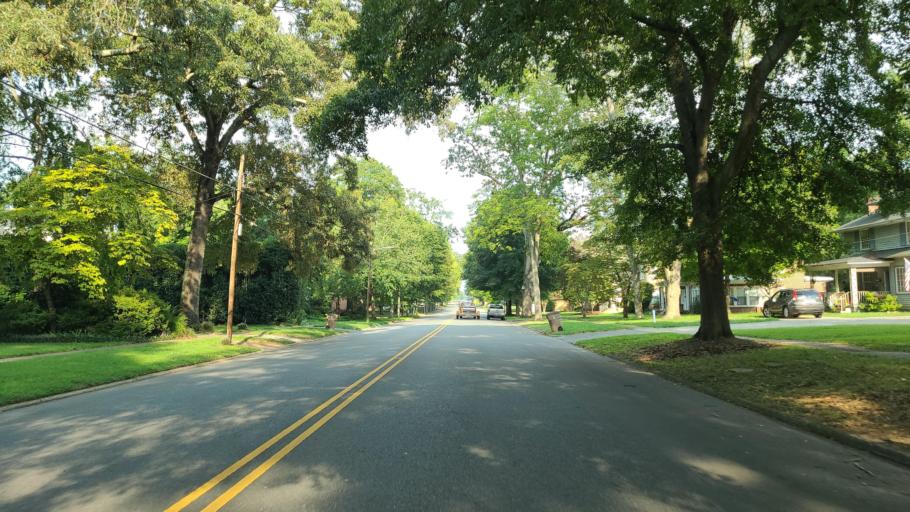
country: US
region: North Carolina
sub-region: Cleveland County
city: Shelby
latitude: 35.2923
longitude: -81.5478
